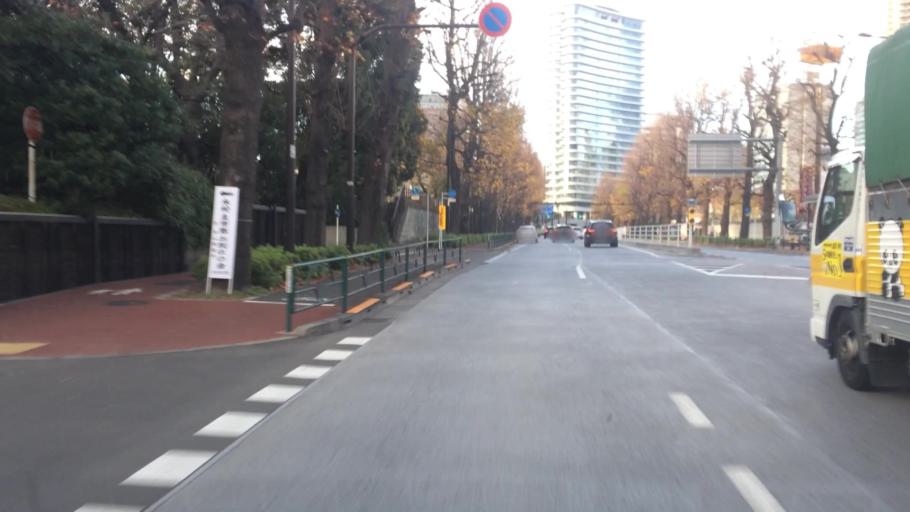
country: JP
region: Tokyo
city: Tokyo
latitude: 35.6670
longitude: 139.7243
